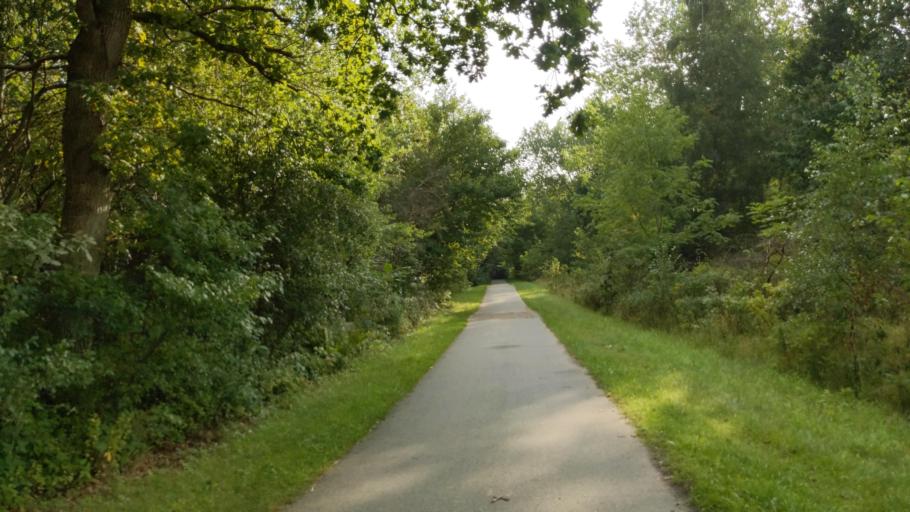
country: DE
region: Mecklenburg-Vorpommern
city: Dassow
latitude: 53.9826
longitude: 10.9722
